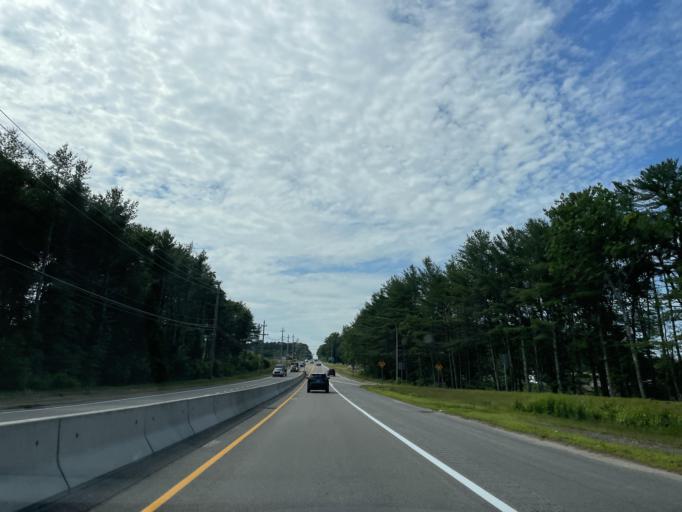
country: US
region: Rhode Island
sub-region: Kent County
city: West Greenwich
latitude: 41.6059
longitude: -71.6600
